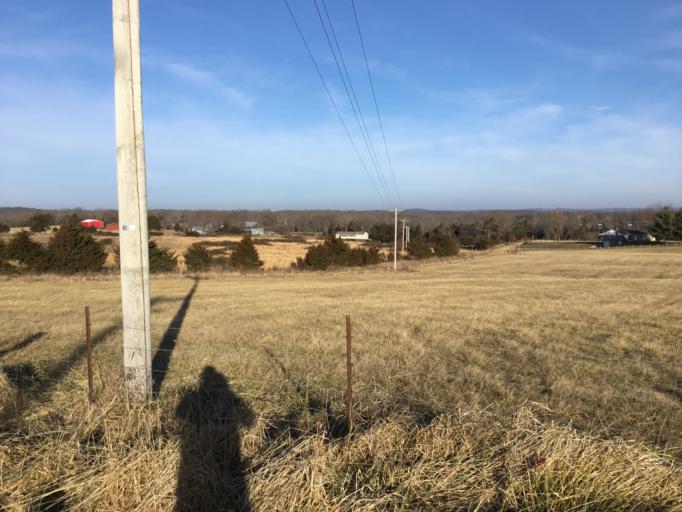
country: US
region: Missouri
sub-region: Osage County
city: Linn
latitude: 38.3478
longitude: -91.8756
